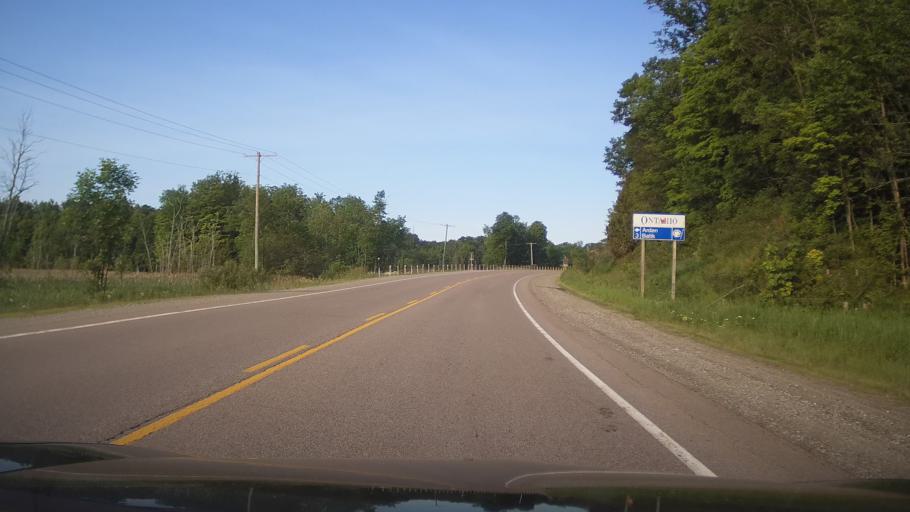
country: CA
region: Ontario
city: Skatepark
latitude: 44.7417
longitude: -76.9257
